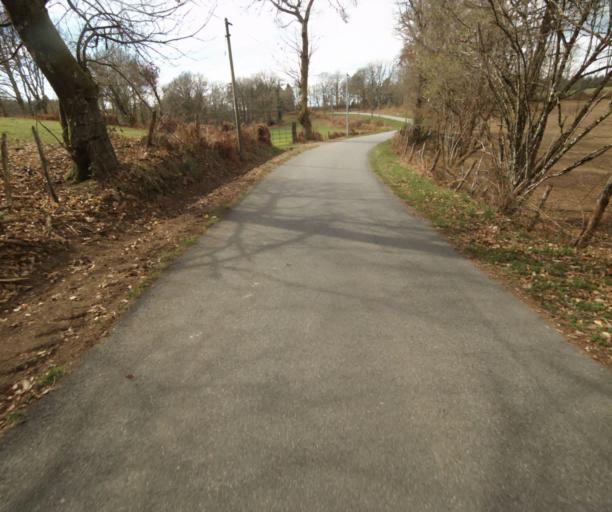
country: FR
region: Limousin
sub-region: Departement de la Correze
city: Correze
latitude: 45.3916
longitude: 1.8989
